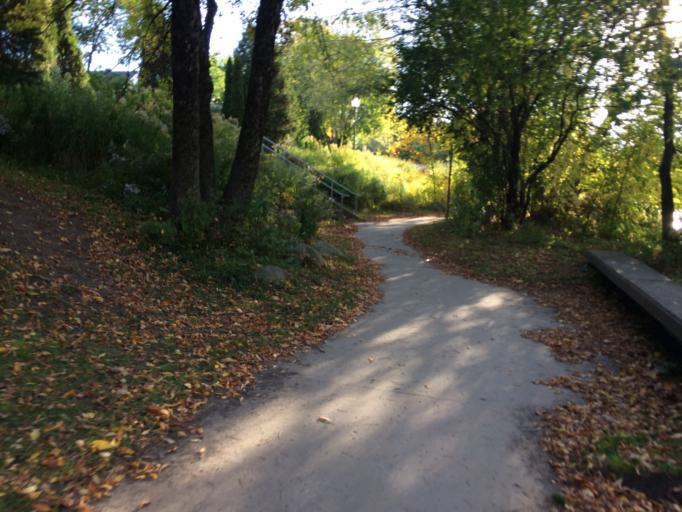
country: CA
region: Quebec
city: Quebec
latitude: 46.8099
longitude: -71.2540
